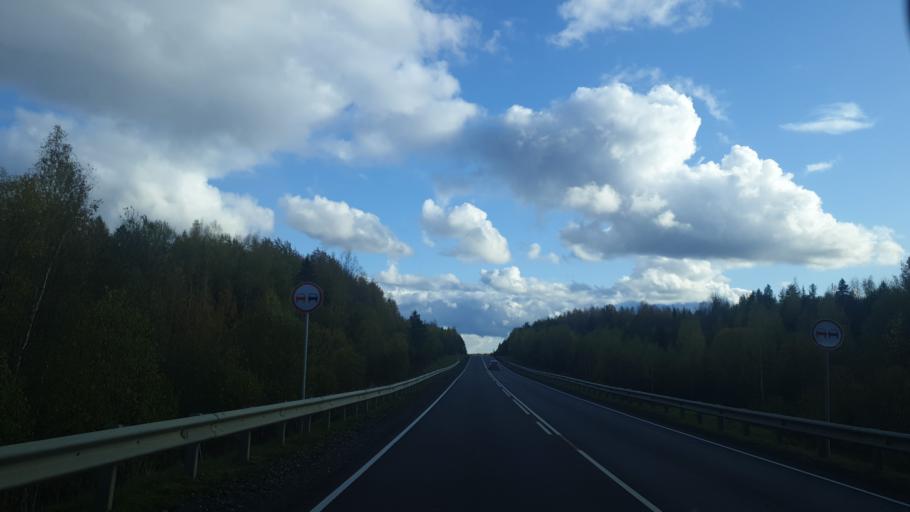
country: RU
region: Komi Republic
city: Letka
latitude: 59.7016
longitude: 49.3814
